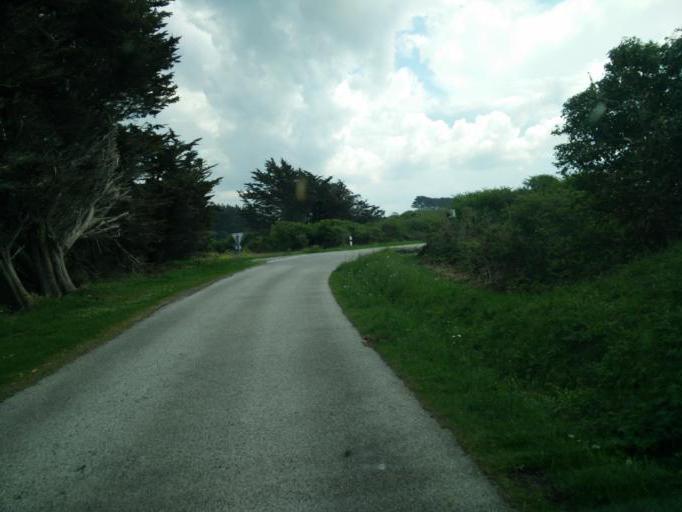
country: FR
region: Brittany
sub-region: Departement du Finistere
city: Roscanvel
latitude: 48.3163
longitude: -4.5724
